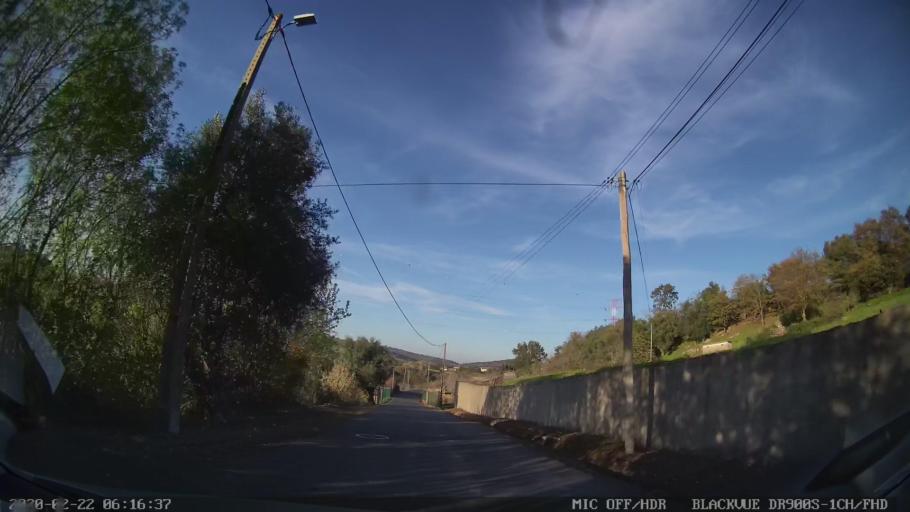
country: PT
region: Lisbon
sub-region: Vila Franca de Xira
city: Castanheira do Ribatejo
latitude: 38.9920
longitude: -9.0168
